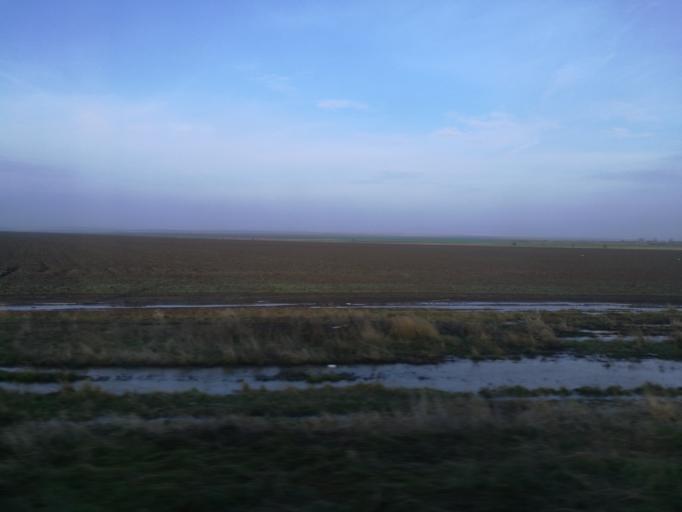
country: RO
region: Buzau
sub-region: Comuna Cochirleanca
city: Cochirleanca
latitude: 45.2726
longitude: 27.0020
